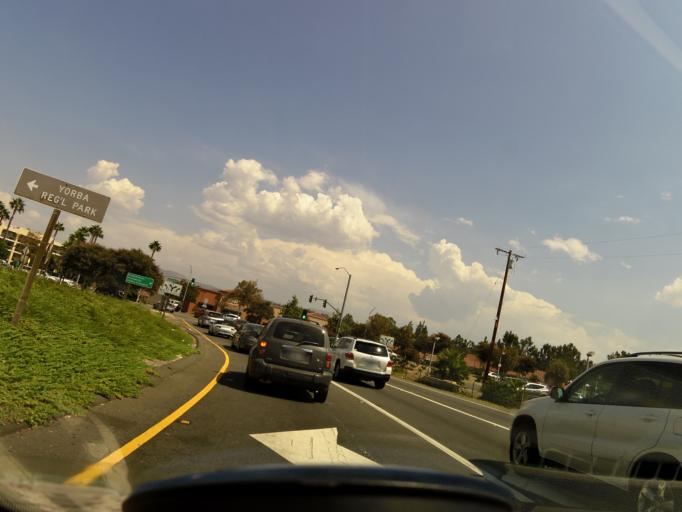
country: US
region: California
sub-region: Orange County
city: Yorba Linda
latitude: 33.8532
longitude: -117.7915
